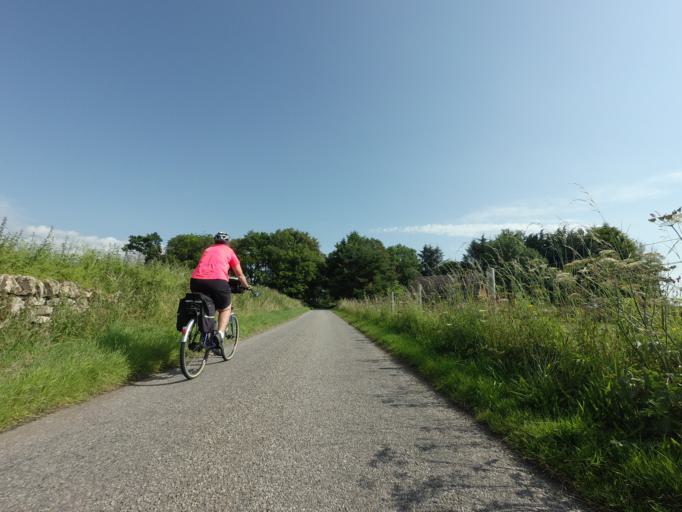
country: GB
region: Scotland
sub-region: Highland
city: Alness
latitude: 57.7120
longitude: -4.2229
